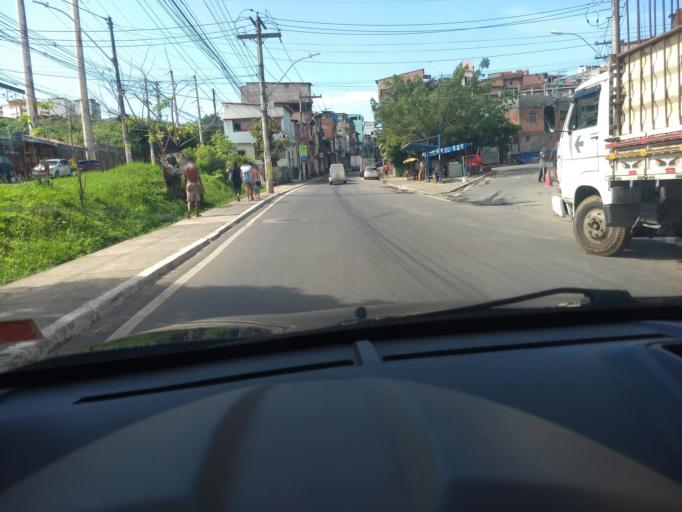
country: BR
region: Bahia
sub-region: Salvador
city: Salvador
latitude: -12.9542
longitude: -38.4459
